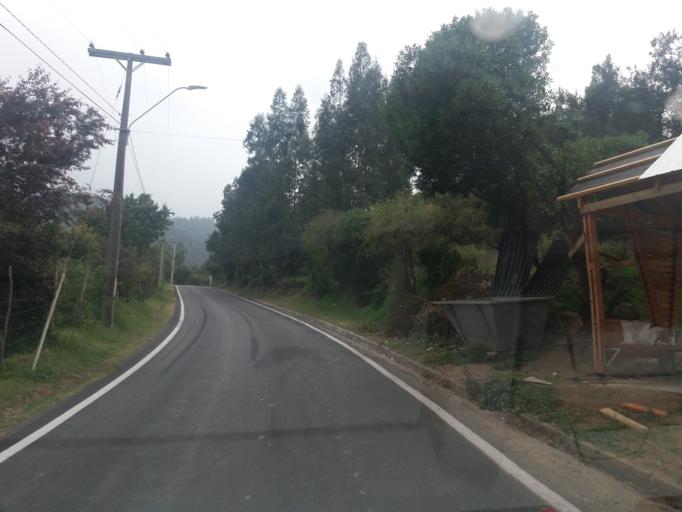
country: CL
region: Valparaiso
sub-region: Provincia de Marga Marga
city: Limache
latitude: -33.0285
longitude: -71.0785
